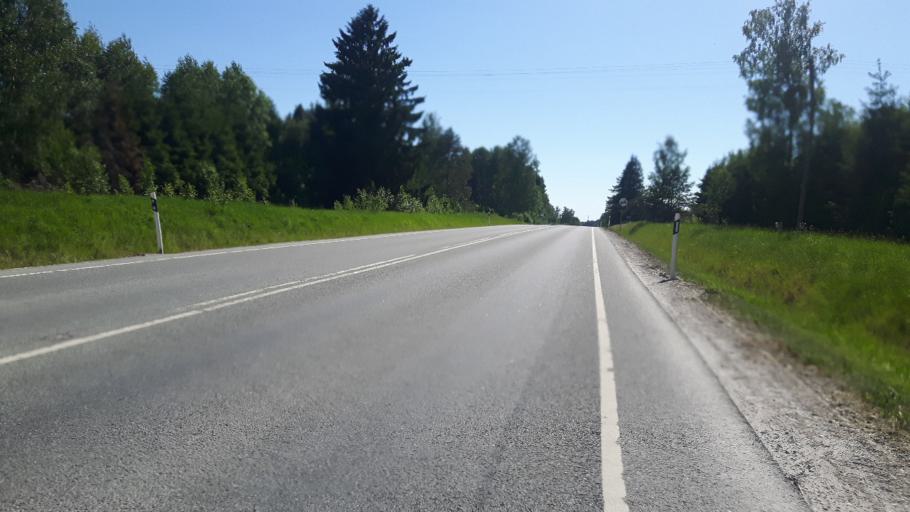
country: EE
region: Raplamaa
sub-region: Rapla vald
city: Rapla
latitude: 59.0363
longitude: 24.8311
